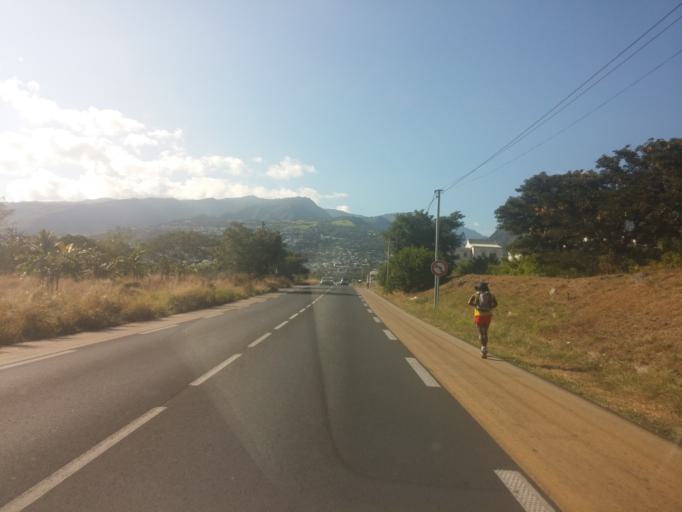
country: RE
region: Reunion
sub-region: Reunion
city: Le Port
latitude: -20.9577
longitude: 55.3163
